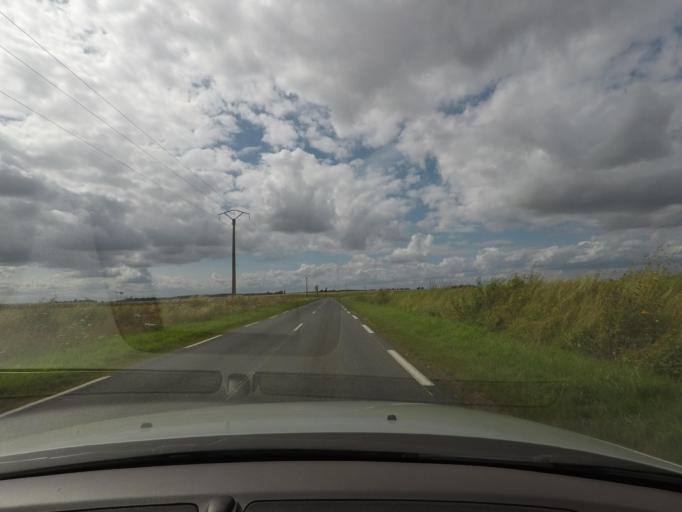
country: FR
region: Haute-Normandie
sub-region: Departement de l'Eure
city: Les Andelys
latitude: 49.2238
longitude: 1.4439
